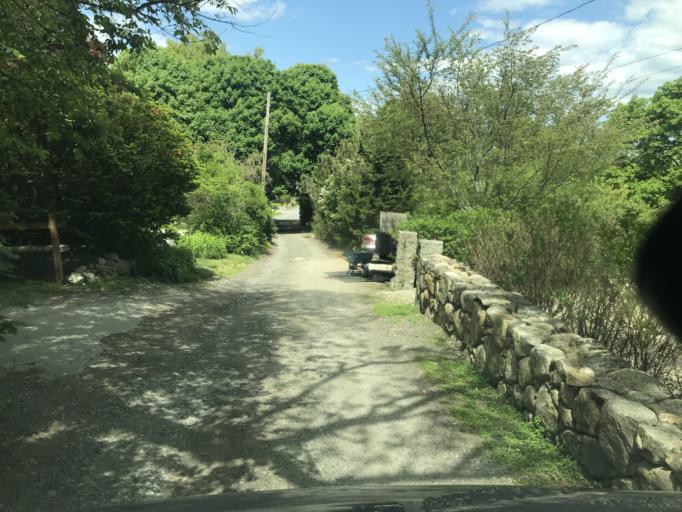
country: US
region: Massachusetts
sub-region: Essex County
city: Rockport
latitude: 42.6558
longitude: -70.6100
